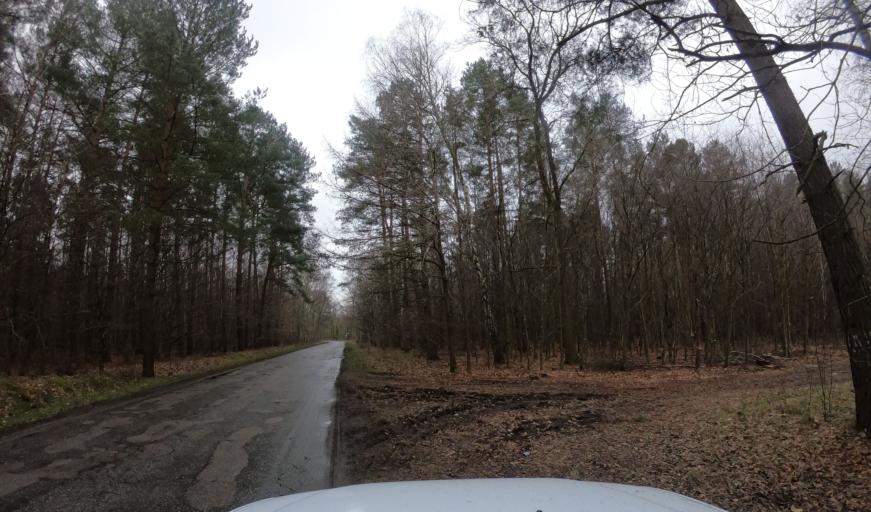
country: PL
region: West Pomeranian Voivodeship
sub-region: Powiat kamienski
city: Swierzno
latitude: 53.9386
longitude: 14.9152
